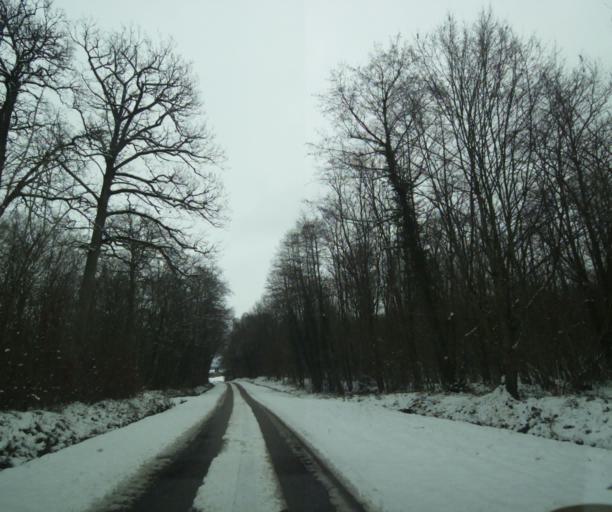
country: FR
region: Champagne-Ardenne
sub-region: Departement de la Haute-Marne
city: Montier-en-Der
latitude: 48.4206
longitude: 4.7806
